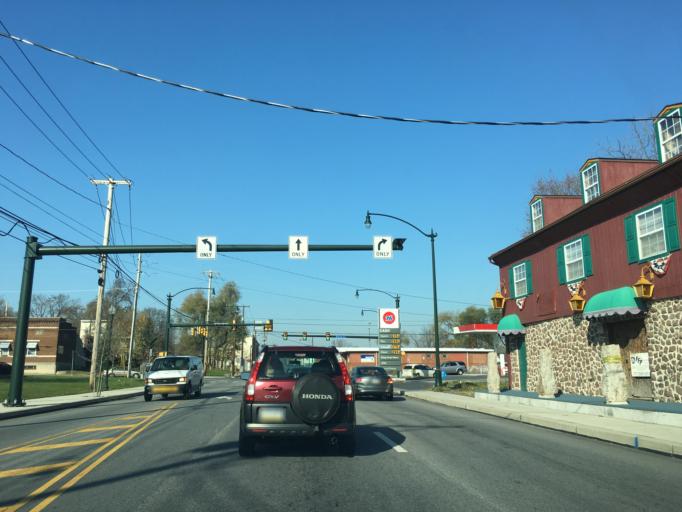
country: US
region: Pennsylvania
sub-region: Dauphin County
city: Harrisburg
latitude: 40.2804
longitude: -76.8881
